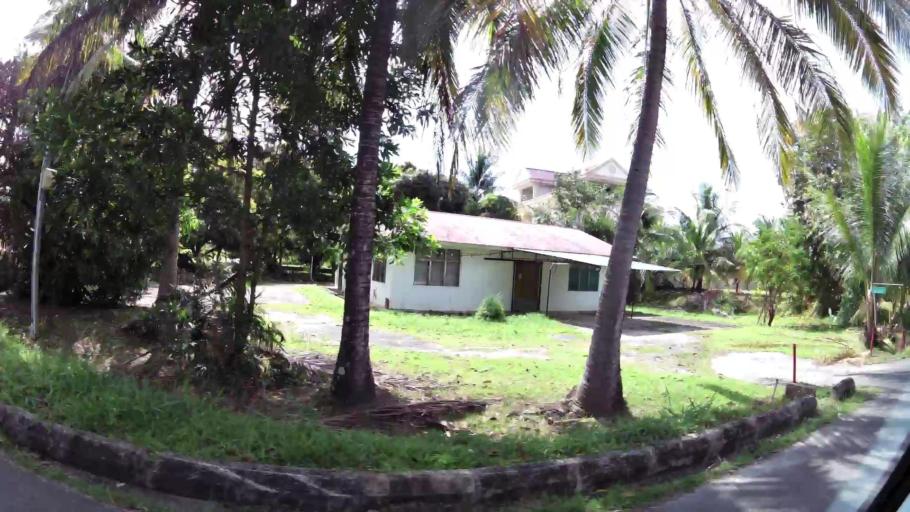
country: BN
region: Brunei and Muara
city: Bandar Seri Begawan
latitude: 4.9534
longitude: 114.9589
